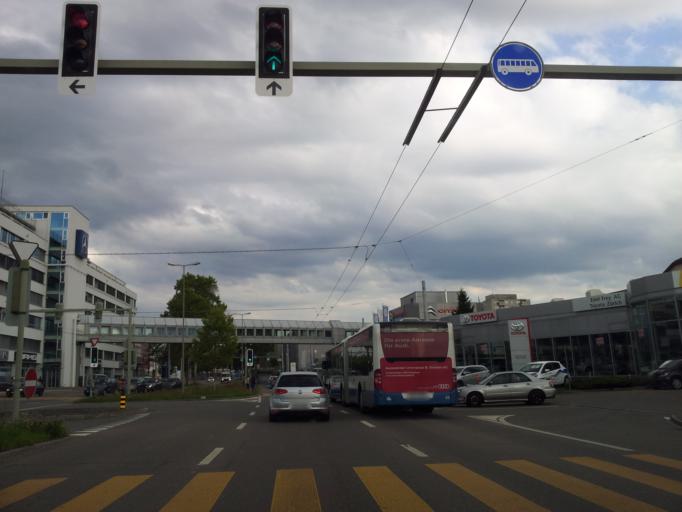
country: CH
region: Zurich
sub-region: Bezirk Dietikon
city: Schlieren / Boden
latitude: 47.3977
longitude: 8.4604
